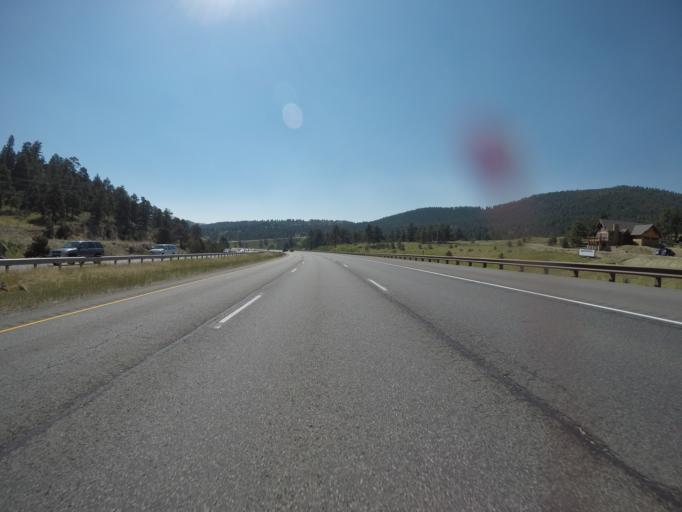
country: US
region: Colorado
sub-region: Jefferson County
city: Evergreen
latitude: 39.7167
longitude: -105.3980
